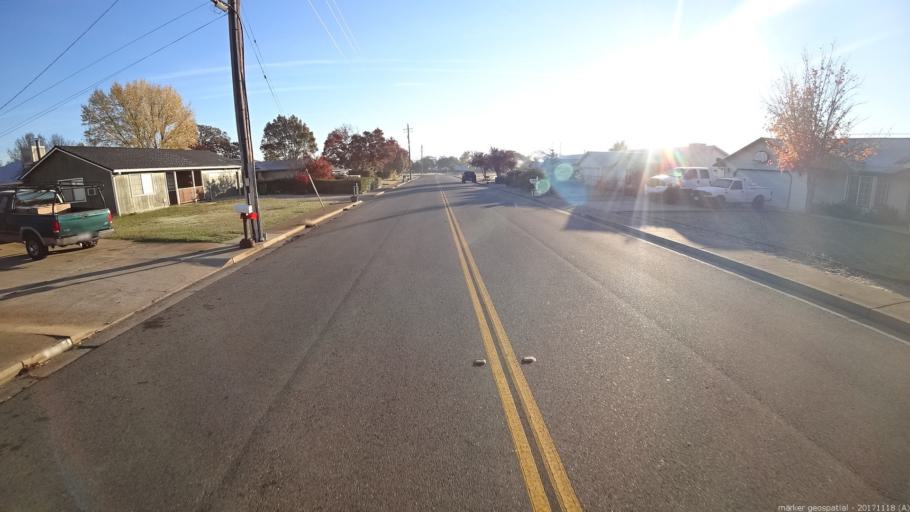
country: US
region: California
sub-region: Shasta County
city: Cottonwood
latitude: 40.3977
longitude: -122.2858
